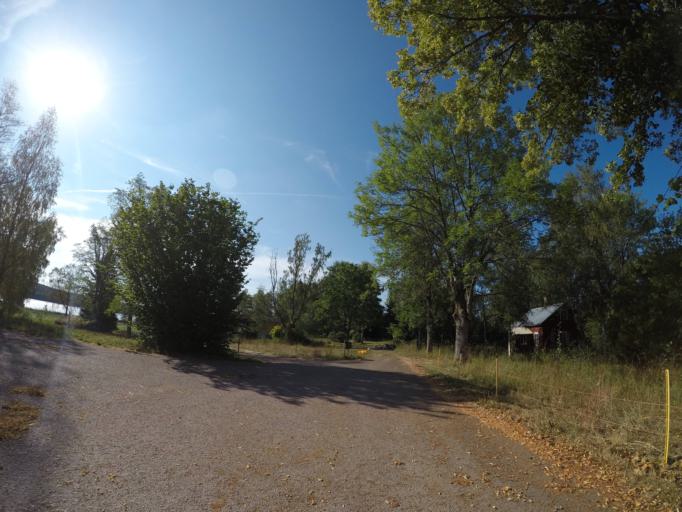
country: AX
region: Alands landsbygd
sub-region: Finstroem
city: Finstroem
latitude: 60.2466
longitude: 19.9217
